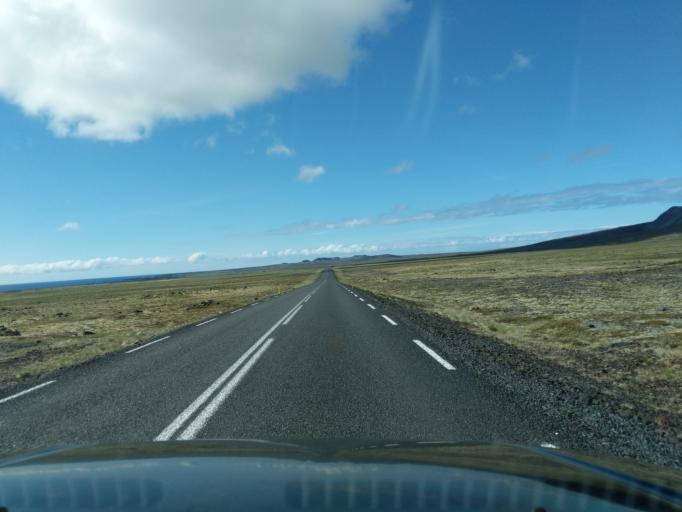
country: IS
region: West
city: Olafsvik
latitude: 64.7899
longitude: -23.9114
